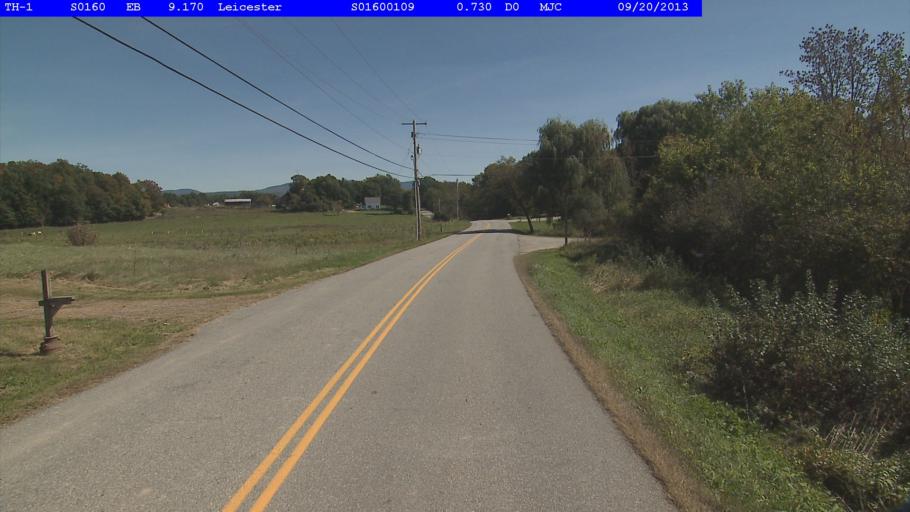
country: US
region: Vermont
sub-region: Rutland County
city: Brandon
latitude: 43.8554
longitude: -73.1454
